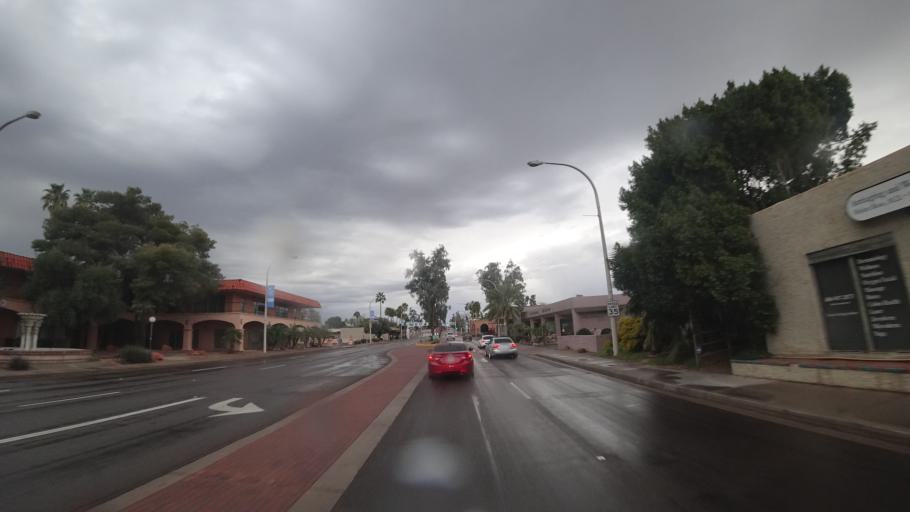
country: US
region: Arizona
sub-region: Maricopa County
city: Scottsdale
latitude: 33.4953
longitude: -111.9304
